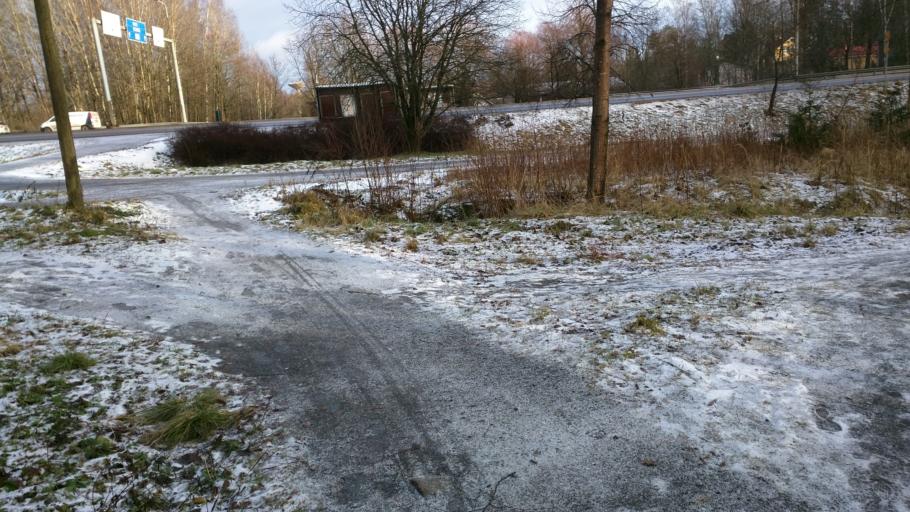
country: FI
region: Uusimaa
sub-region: Helsinki
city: Kilo
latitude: 60.2630
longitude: 24.8101
